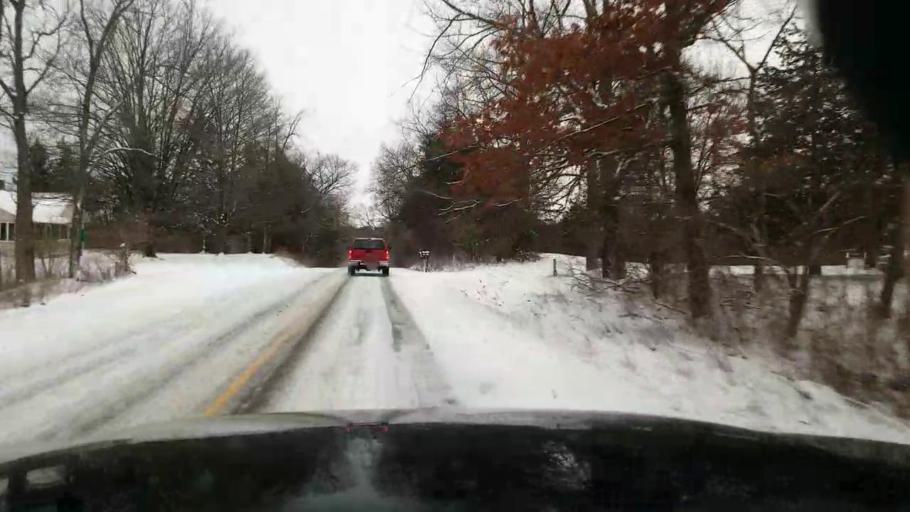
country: US
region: Michigan
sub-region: Jackson County
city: Spring Arbor
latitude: 42.1323
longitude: -84.4985
